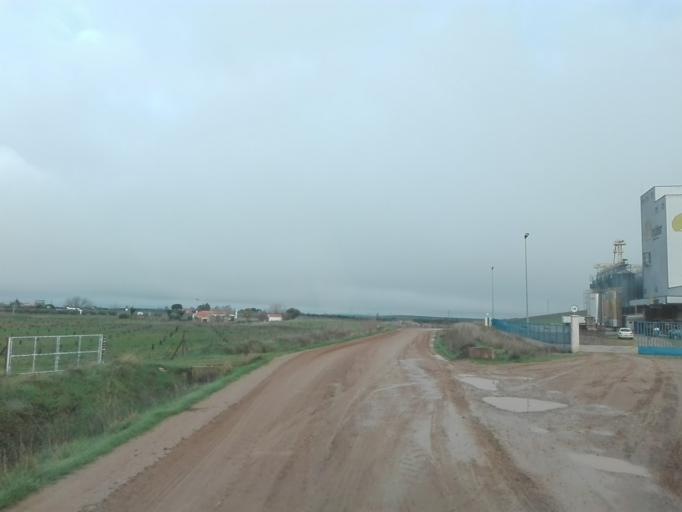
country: ES
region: Extremadura
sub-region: Provincia de Badajoz
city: Llerena
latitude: 38.2561
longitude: -6.0293
